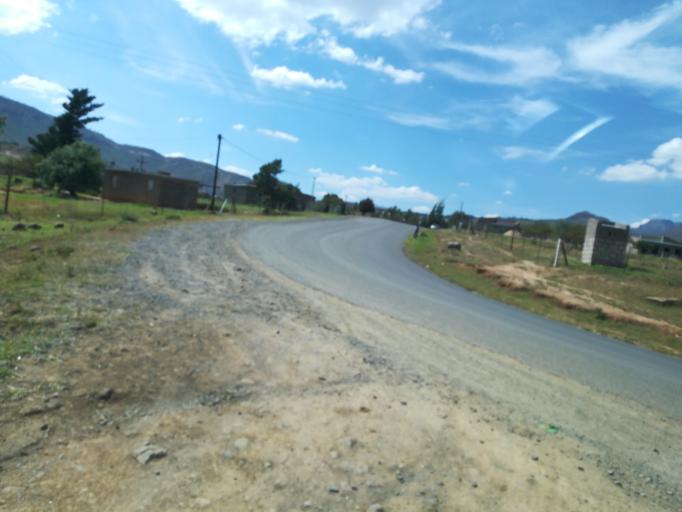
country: LS
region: Mohale's Hoek District
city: Mohale's Hoek
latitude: -30.1086
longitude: 27.4683
